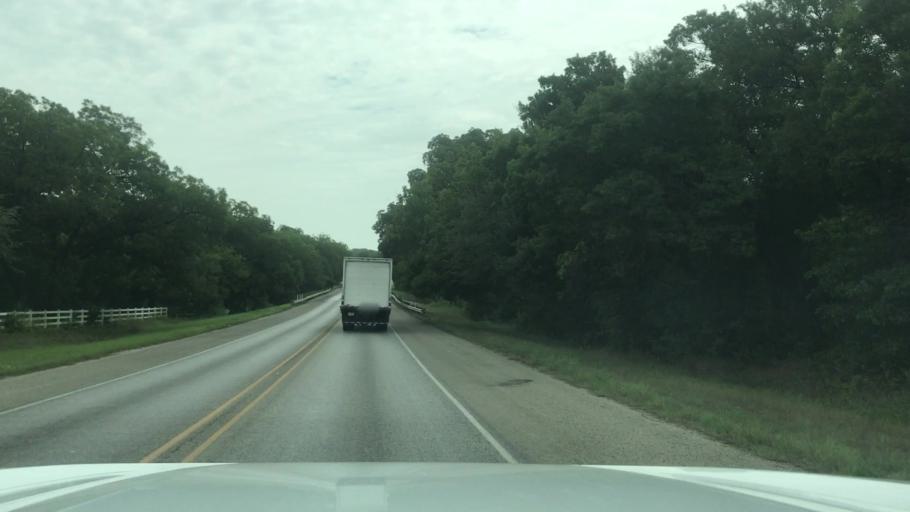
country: US
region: Texas
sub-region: Comanche County
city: De Leon
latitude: 32.1034
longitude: -98.4828
